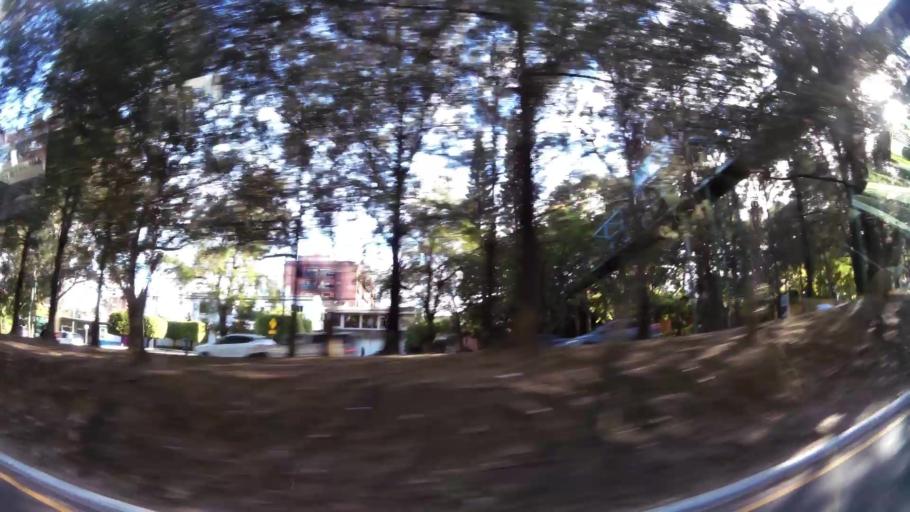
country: GT
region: Guatemala
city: Santa Catarina Pinula
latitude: 14.5919
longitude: -90.4927
